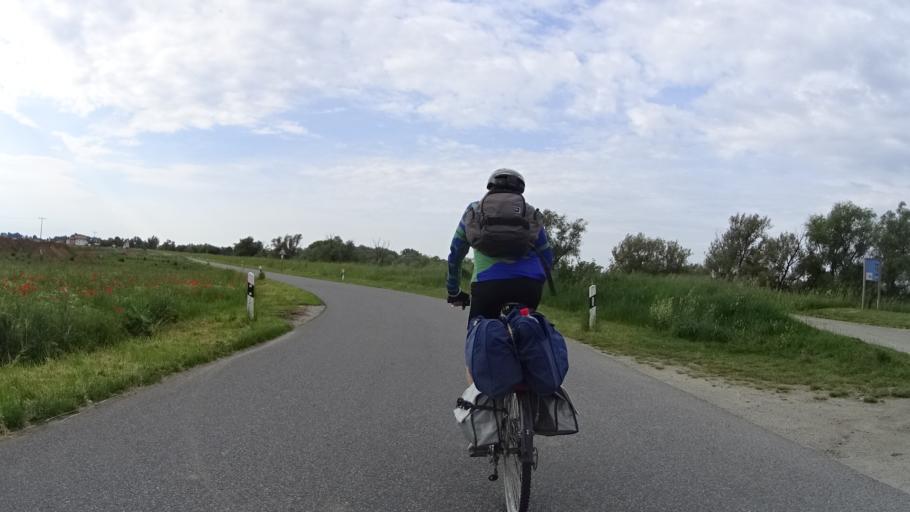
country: DE
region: Bavaria
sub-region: Lower Bavaria
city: Irlbach
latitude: 48.8761
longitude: 12.7535
